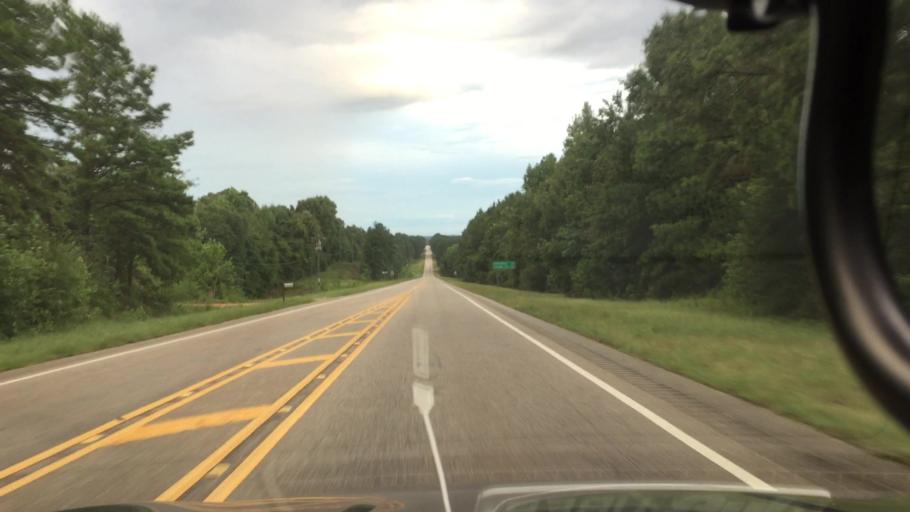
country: US
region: Alabama
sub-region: Pike County
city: Troy
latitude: 31.6746
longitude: -85.9564
